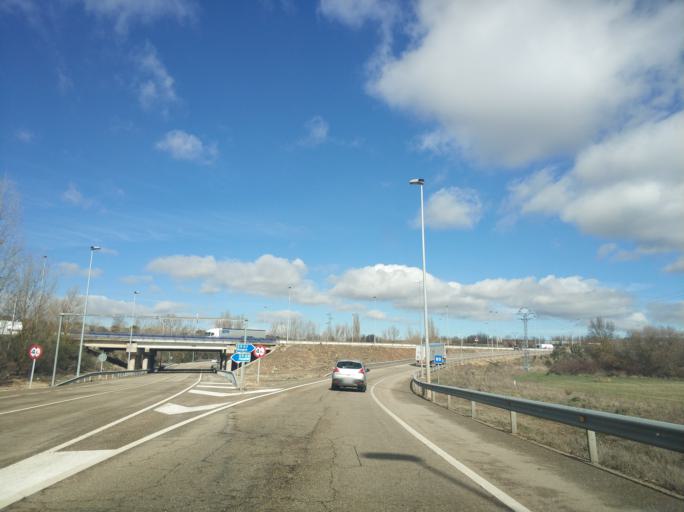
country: ES
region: Castille and Leon
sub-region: Provincia de Burgos
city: Saldana de Burgos
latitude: 42.2628
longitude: -3.6979
